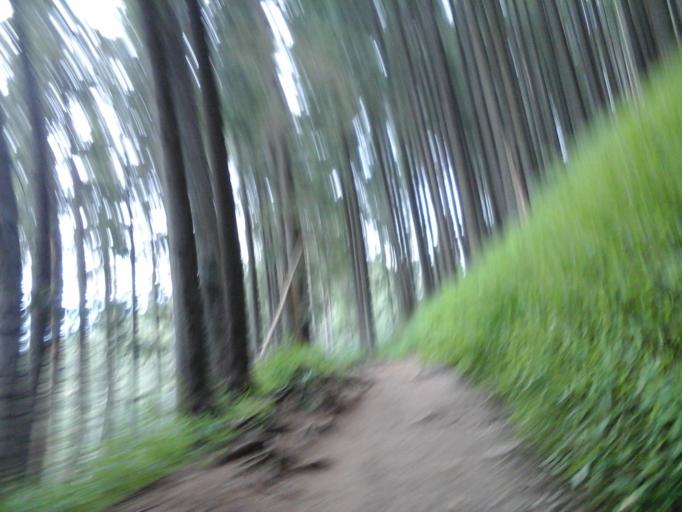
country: PL
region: Lesser Poland Voivodeship
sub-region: Powiat tatrzanski
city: Zakopane
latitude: 49.2706
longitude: 19.9875
